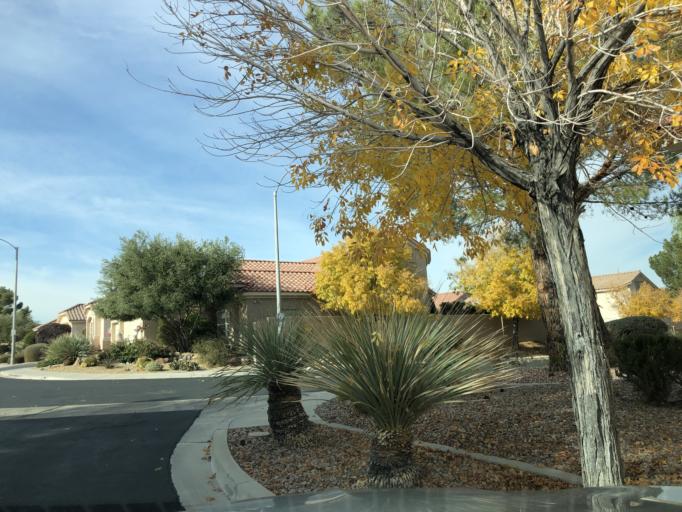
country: US
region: Nevada
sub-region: Clark County
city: Whitney
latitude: 36.0134
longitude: -115.0836
